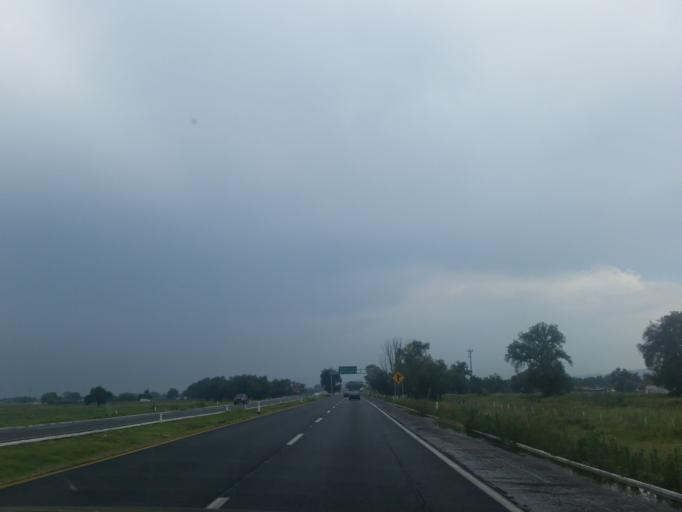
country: MX
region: Mexico
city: Acolman
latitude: 19.6327
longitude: -98.9084
